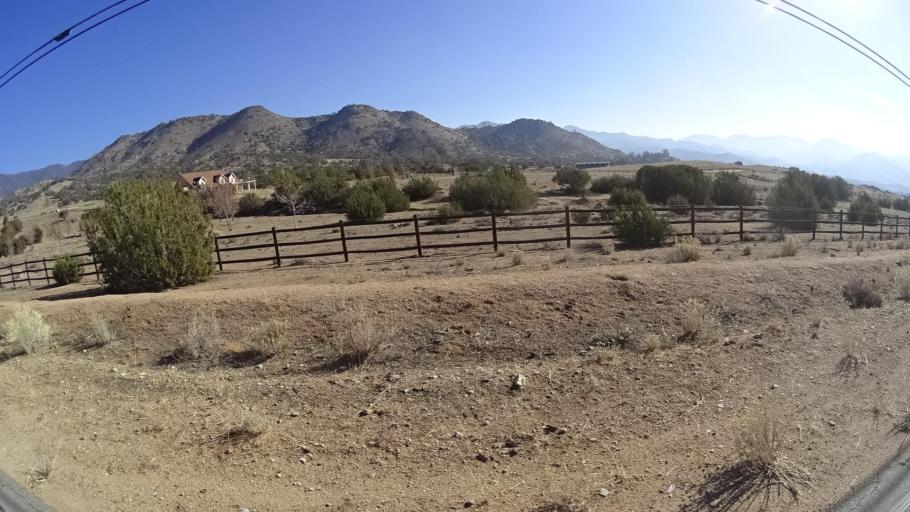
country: US
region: California
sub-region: Kern County
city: Tehachapi
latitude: 35.3558
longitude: -118.3838
